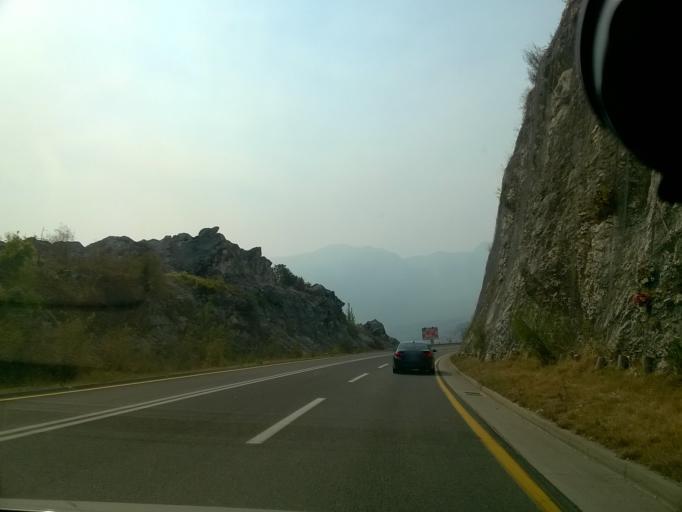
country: ME
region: Bar
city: Sutomore
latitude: 42.2199
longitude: 19.0516
